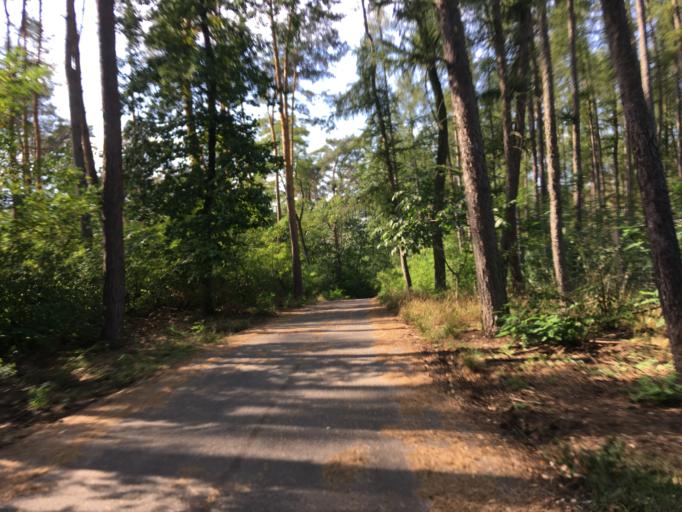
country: DE
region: Berlin
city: Muggelheim
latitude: 52.4096
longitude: 13.6470
